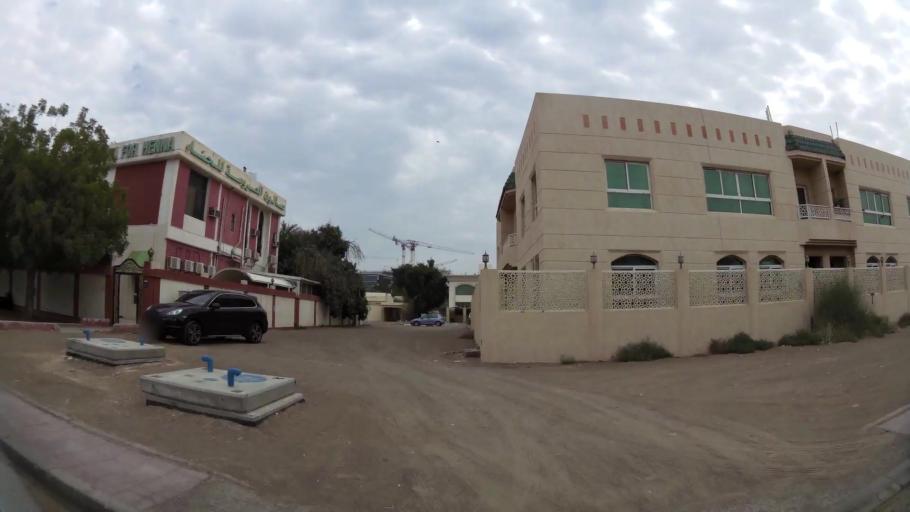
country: AE
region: Abu Dhabi
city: Al Ain
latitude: 24.2280
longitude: 55.7311
